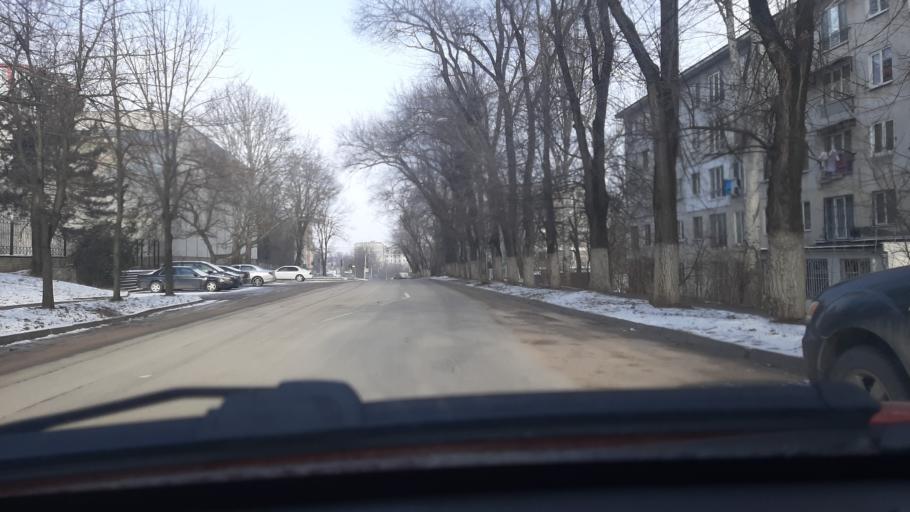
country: MD
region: Chisinau
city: Chisinau
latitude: 47.0018
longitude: 28.8094
